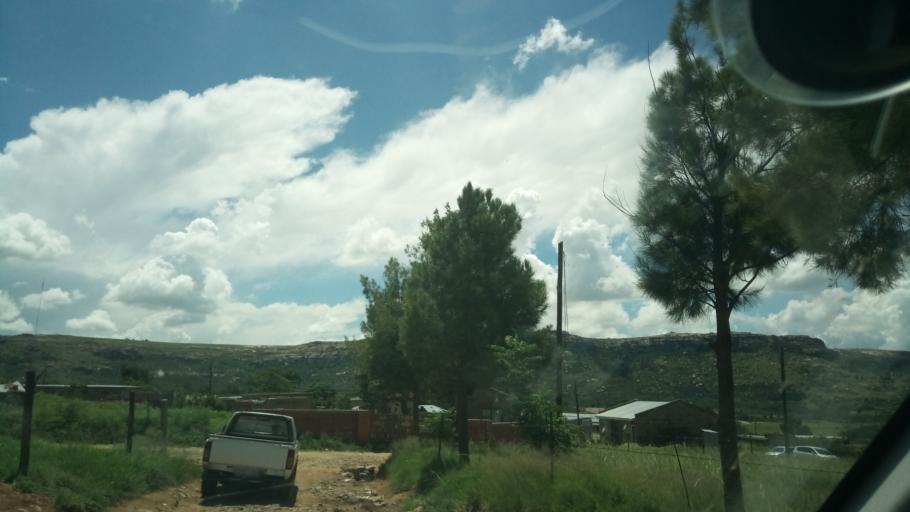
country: LS
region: Maseru
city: Maseru
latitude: -29.3544
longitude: 27.5352
